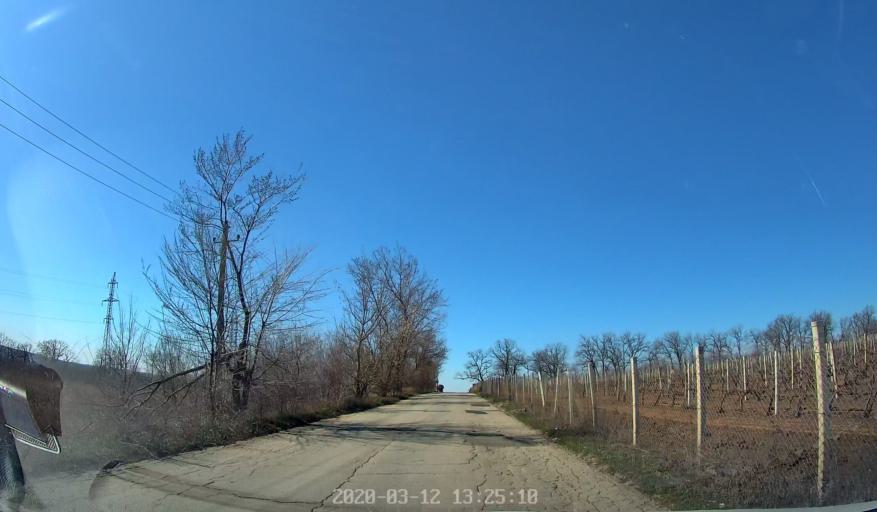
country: MD
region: Laloveni
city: Ialoveni
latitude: 46.9423
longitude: 28.8212
